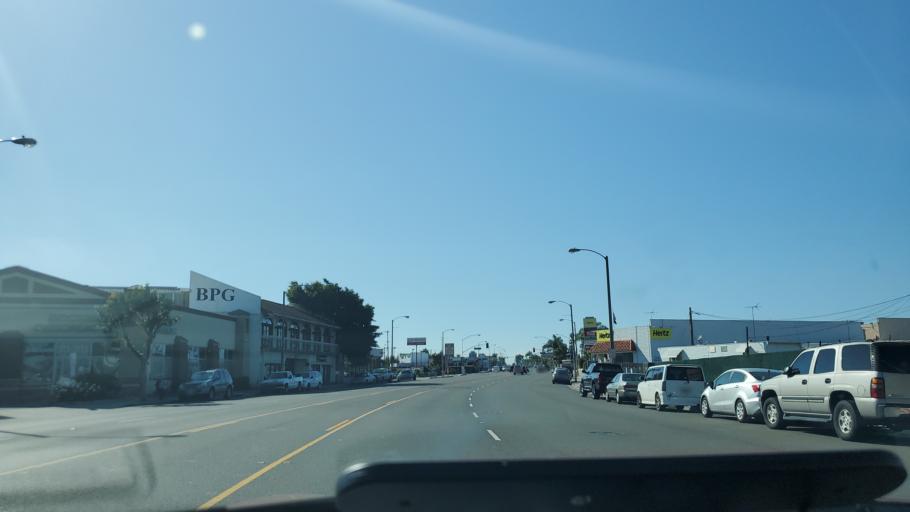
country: US
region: California
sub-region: Los Angeles County
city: Lomita
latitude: 33.7981
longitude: -118.3101
